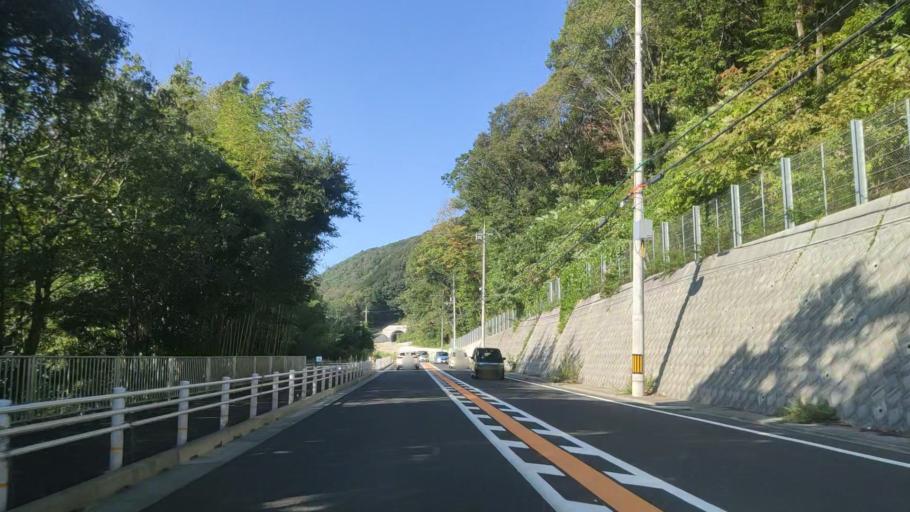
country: JP
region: Hyogo
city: Sandacho
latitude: 34.7955
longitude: 135.2171
